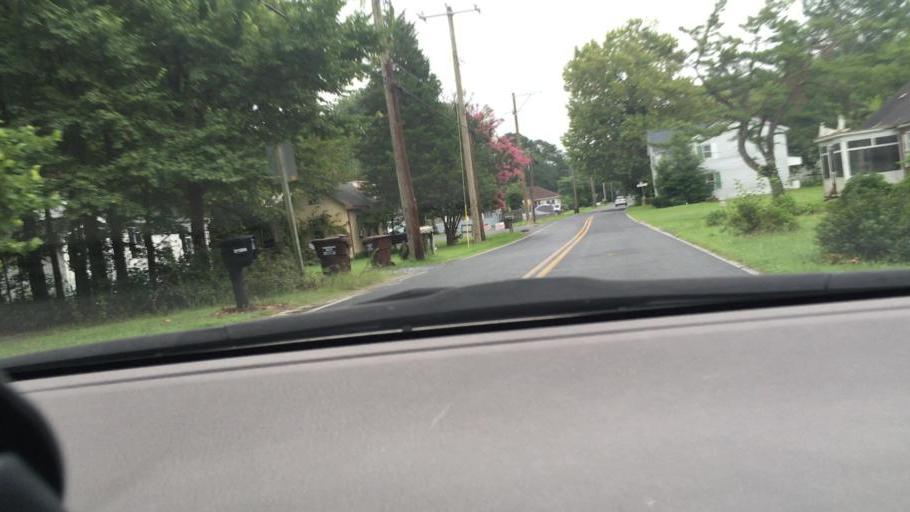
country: US
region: Maryland
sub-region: Wicomico County
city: Fruitland
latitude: 38.3395
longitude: -75.6337
